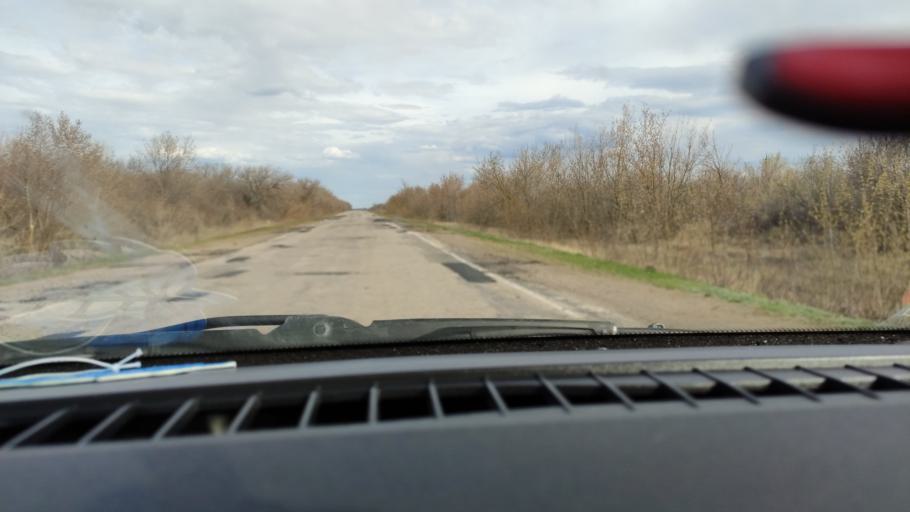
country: RU
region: Saratov
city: Rovnoye
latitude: 51.0691
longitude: 45.9948
